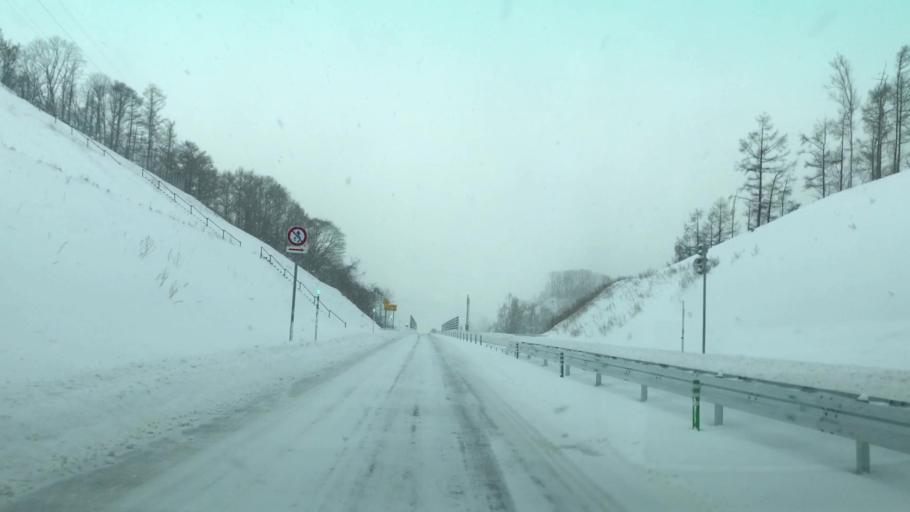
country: JP
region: Hokkaido
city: Otaru
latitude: 43.1969
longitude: 140.9110
